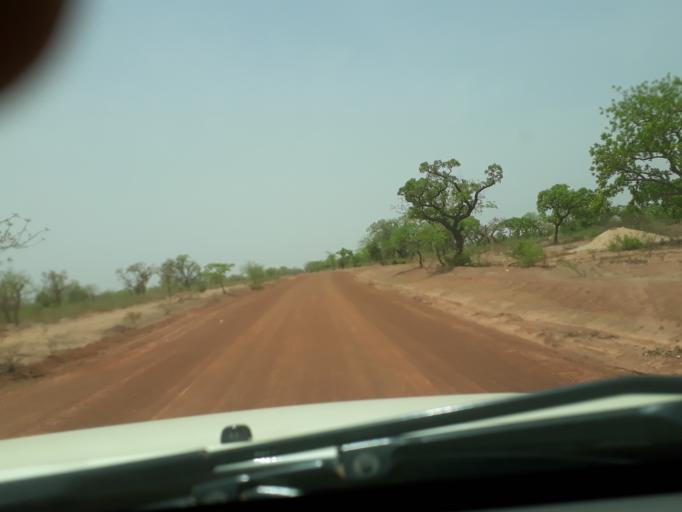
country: BF
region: Plateau-Central
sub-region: Province d'Oubritenga
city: Ziniare
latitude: 12.5809
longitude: -1.3412
